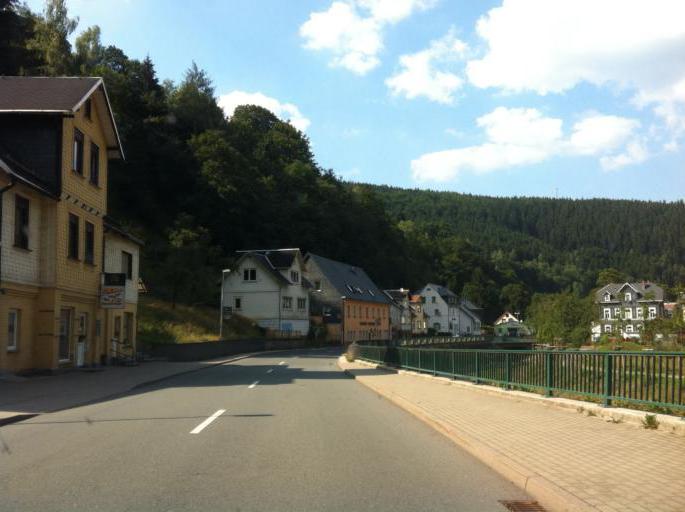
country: DE
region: Thuringia
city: Katzhutte
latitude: 50.5512
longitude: 11.0529
